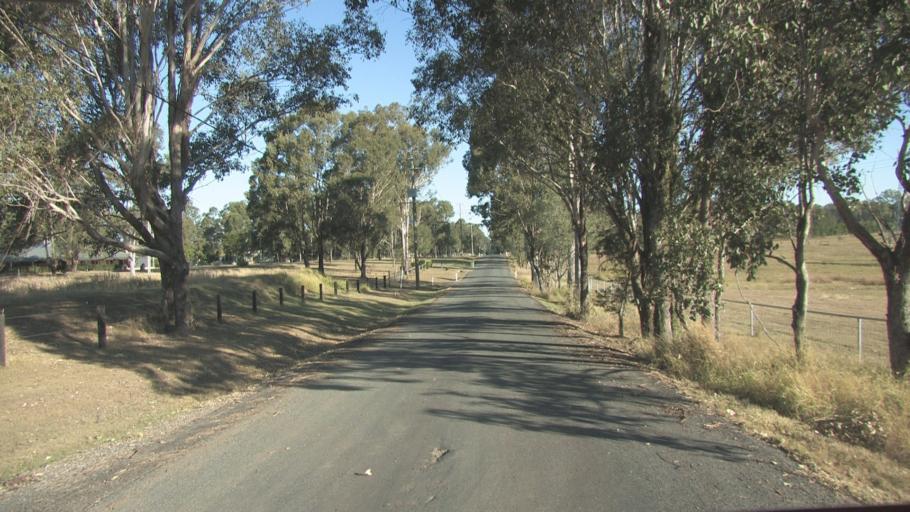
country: AU
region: Queensland
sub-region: Logan
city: North Maclean
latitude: -27.7761
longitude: 153.0474
